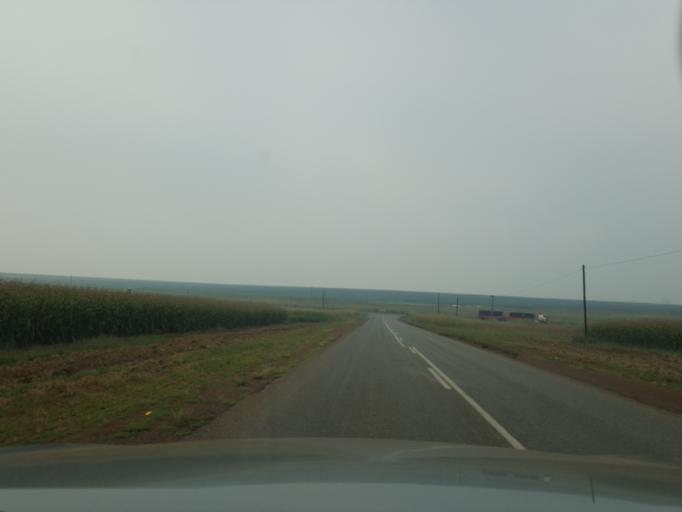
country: ZA
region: Mpumalanga
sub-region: Nkangala District Municipality
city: Middelburg
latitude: -26.0282
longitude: 29.4483
